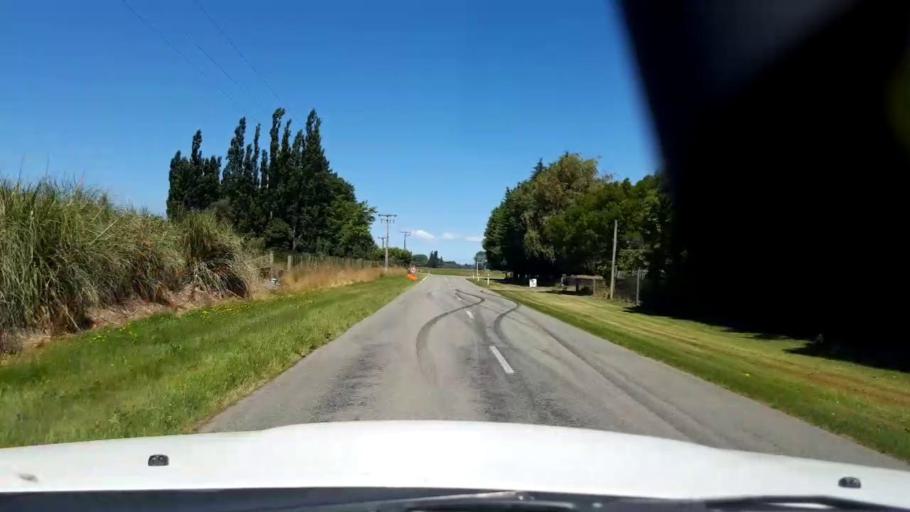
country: NZ
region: Canterbury
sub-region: Timaru District
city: Pleasant Point
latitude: -44.1641
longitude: 171.3068
